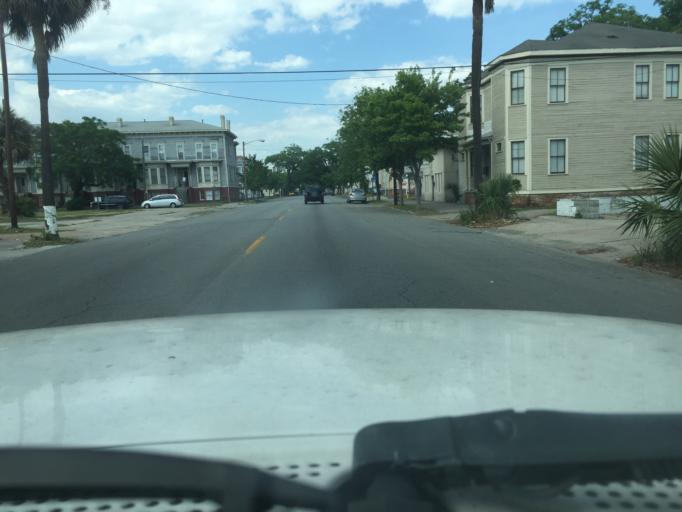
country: US
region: Georgia
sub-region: Chatham County
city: Savannah
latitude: 32.0654
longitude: -81.1018
